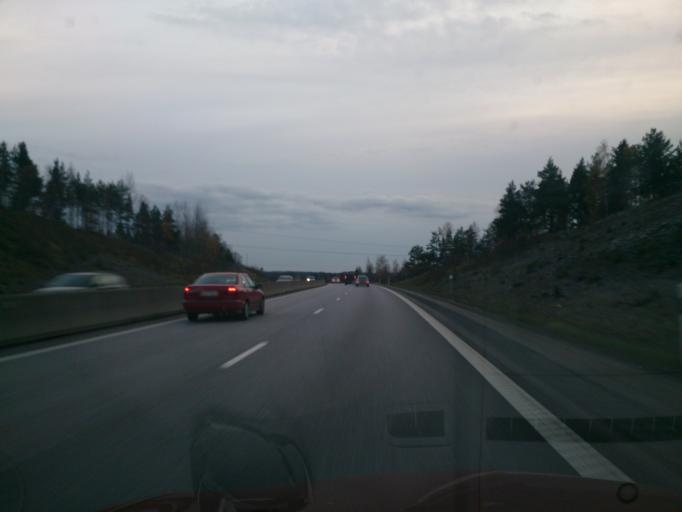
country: SE
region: OEstergoetland
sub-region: Norrkopings Kommun
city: Kimstad
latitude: 58.5149
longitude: 15.9955
